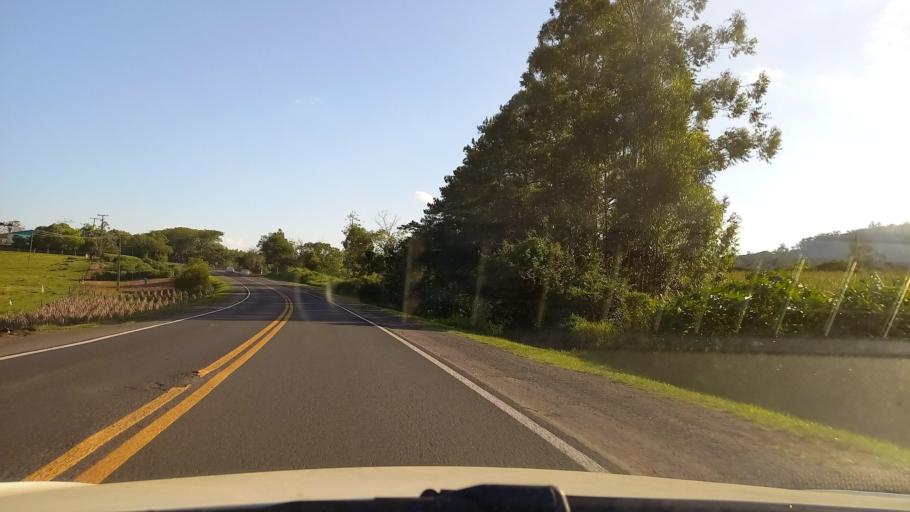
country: BR
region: Rio Grande do Sul
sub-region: Taquari
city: Taquari
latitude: -29.6919
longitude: -51.7446
